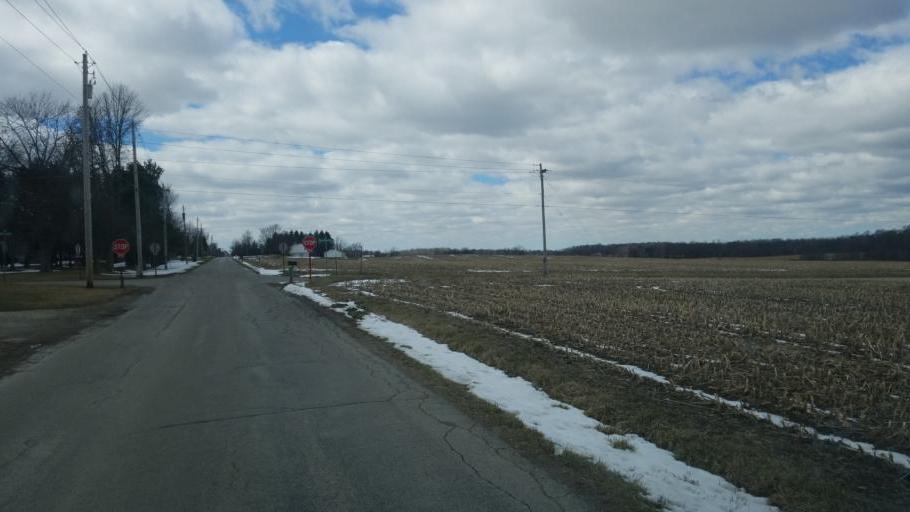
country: US
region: Ohio
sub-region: Richland County
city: Mansfield
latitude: 40.8579
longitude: -82.5513
